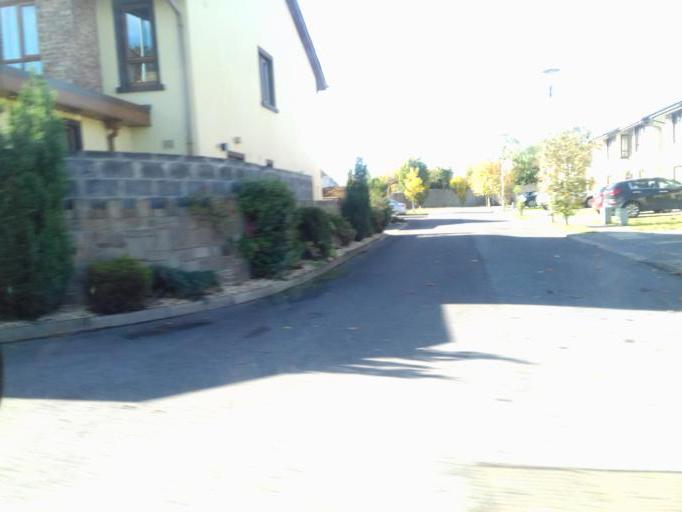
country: IE
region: Leinster
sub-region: An Mhi
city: Ashbourne
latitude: 53.5024
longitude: -6.3897
